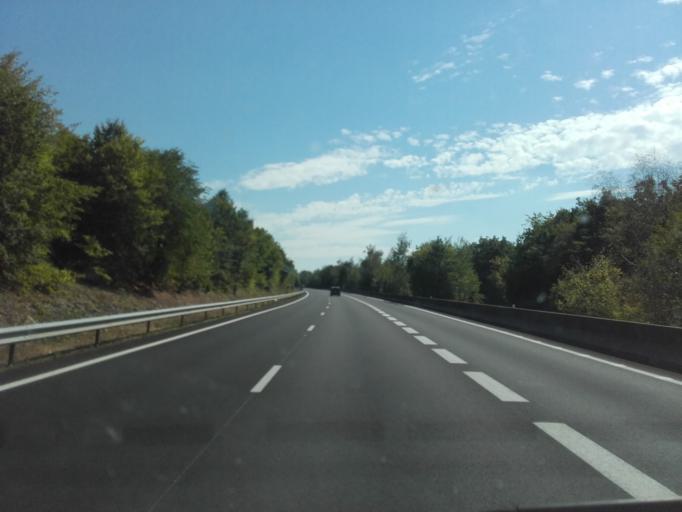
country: FR
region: Bourgogne
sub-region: Departement de la Cote-d'Or
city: Savigny-les-Beaune
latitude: 47.1350
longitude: 4.6994
